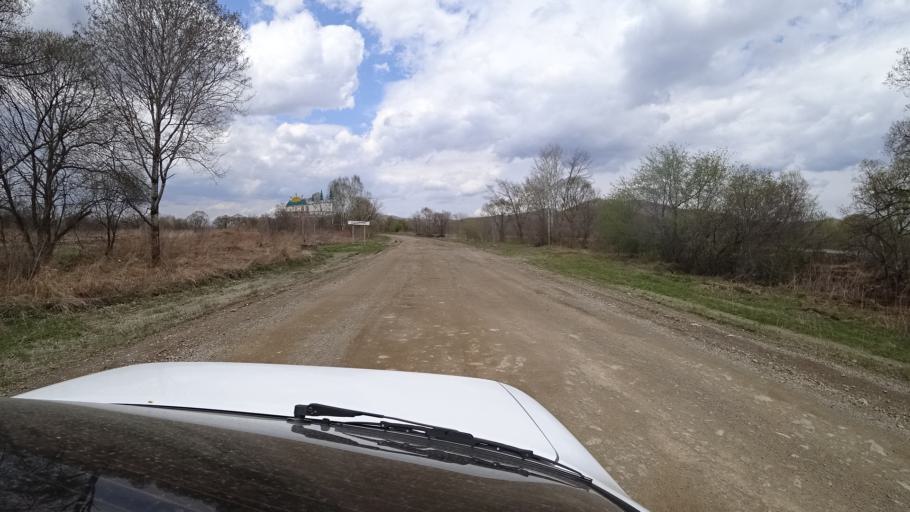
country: RU
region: Primorskiy
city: Novopokrovka
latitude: 45.6122
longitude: 134.2744
